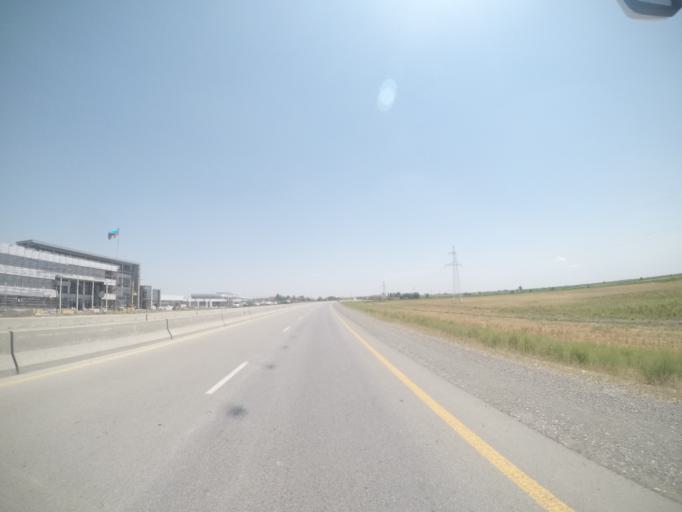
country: AZ
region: Kurdamir Rayon
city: Kyurdarmir
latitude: 40.3216
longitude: 48.1905
